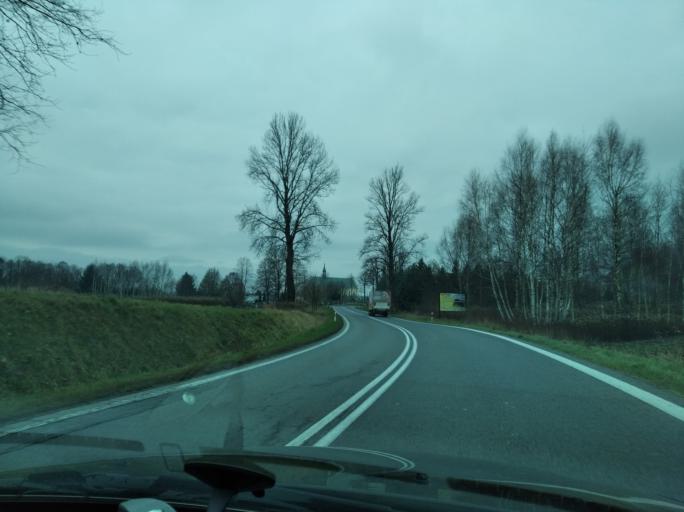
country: PL
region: Subcarpathian Voivodeship
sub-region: Powiat lancucki
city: Zolynia
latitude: 50.1709
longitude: 22.3109
